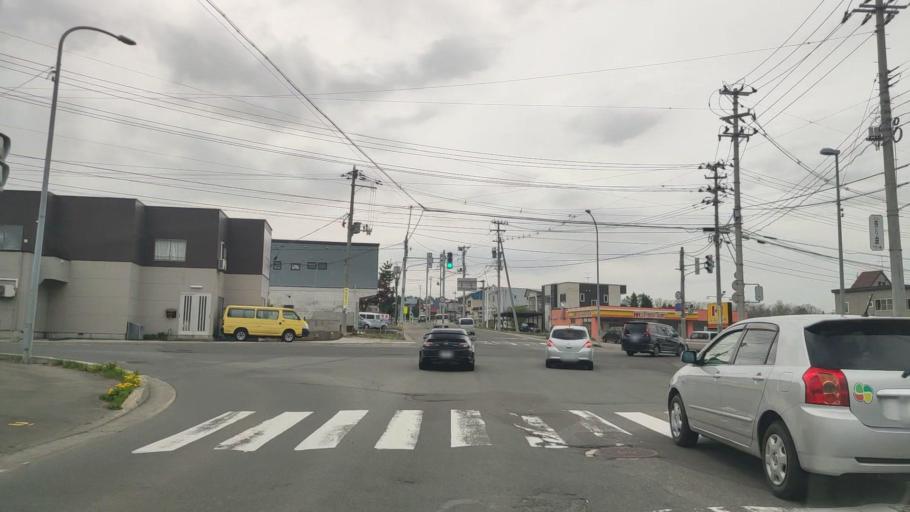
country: JP
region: Aomori
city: Aomori Shi
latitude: 40.7900
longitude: 140.7871
